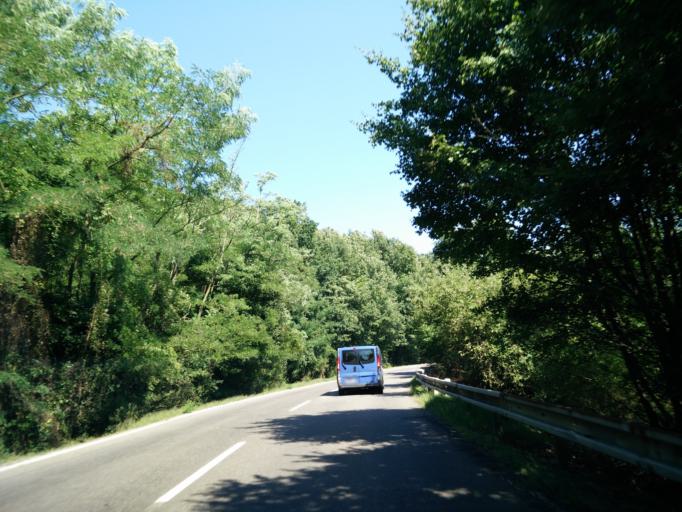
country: SK
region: Banskobystricky
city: Nova Bana
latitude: 48.3734
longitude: 18.5931
